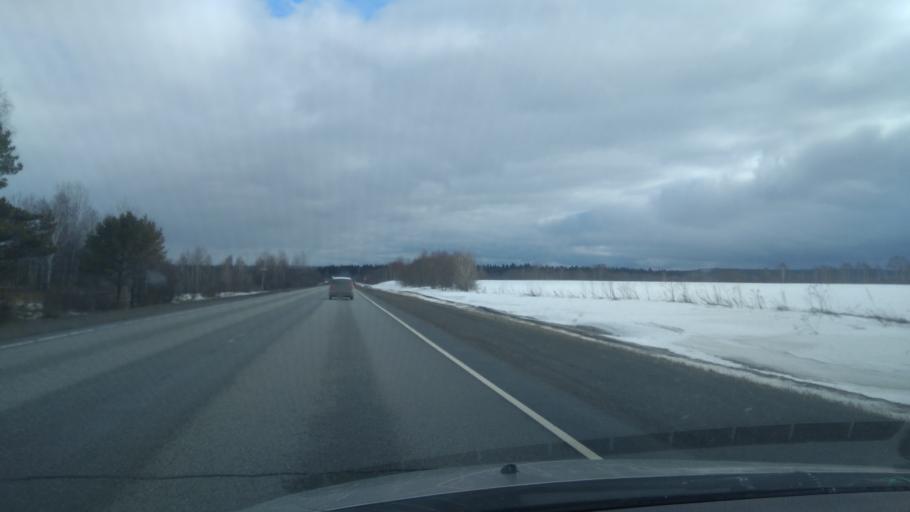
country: RU
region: Sverdlovsk
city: Ufimskiy
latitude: 56.7721
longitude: 58.0758
